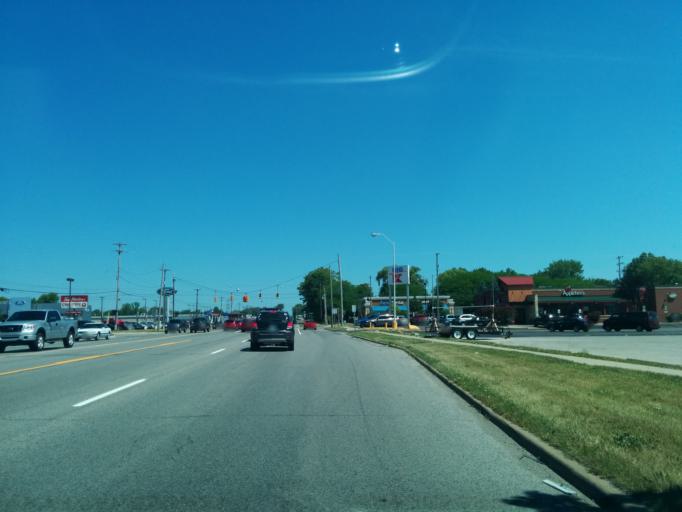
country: US
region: Michigan
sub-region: Bay County
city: Bay City
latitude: 43.6227
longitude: -83.9142
